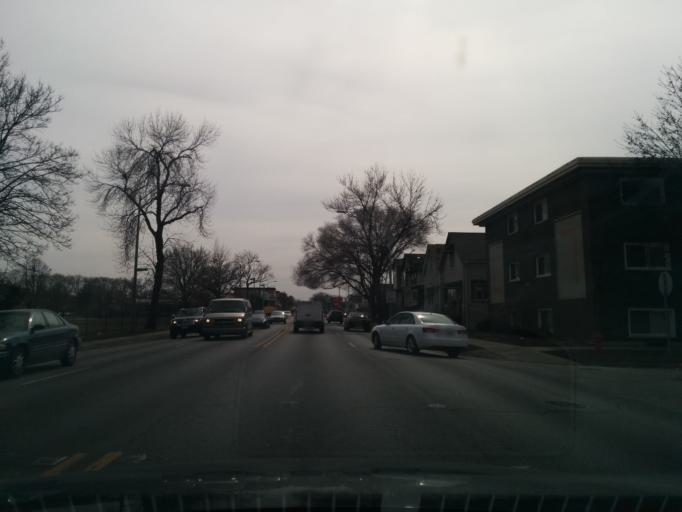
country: US
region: Illinois
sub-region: Cook County
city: Forest Park
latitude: 41.8670
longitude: -87.8043
